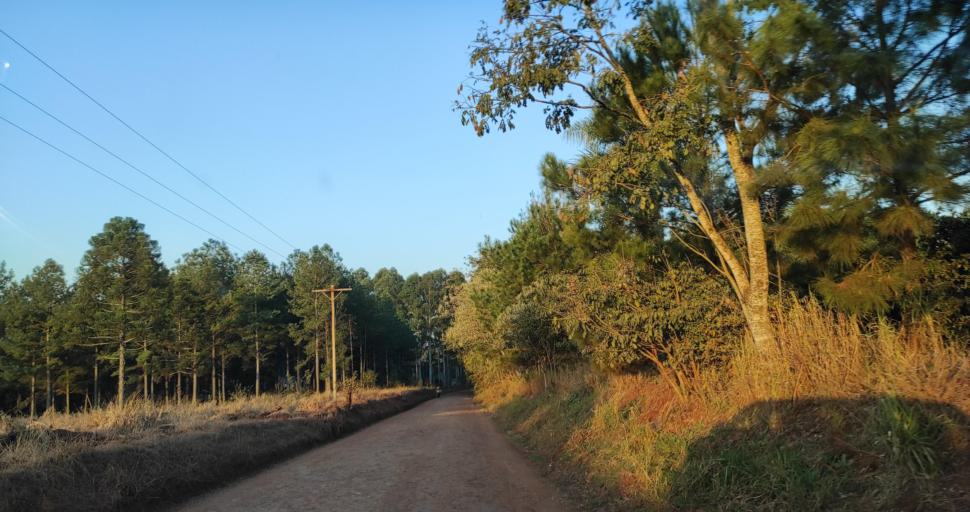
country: AR
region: Misiones
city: Capiovi
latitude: -26.8734
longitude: -55.1061
